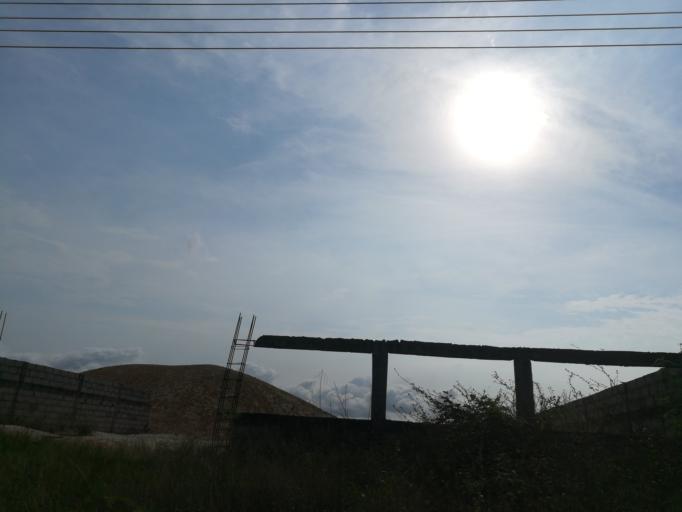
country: NG
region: Rivers
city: Okrika
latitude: 4.7351
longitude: 7.0861
